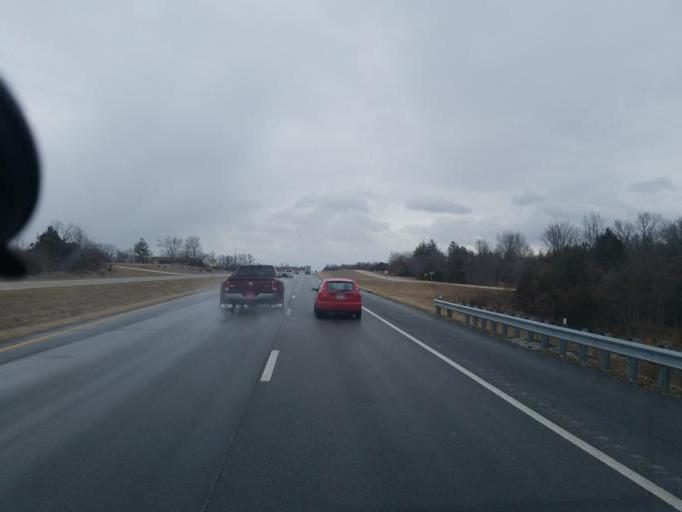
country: US
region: Missouri
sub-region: Randolph County
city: Moberly
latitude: 39.3657
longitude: -92.4060
